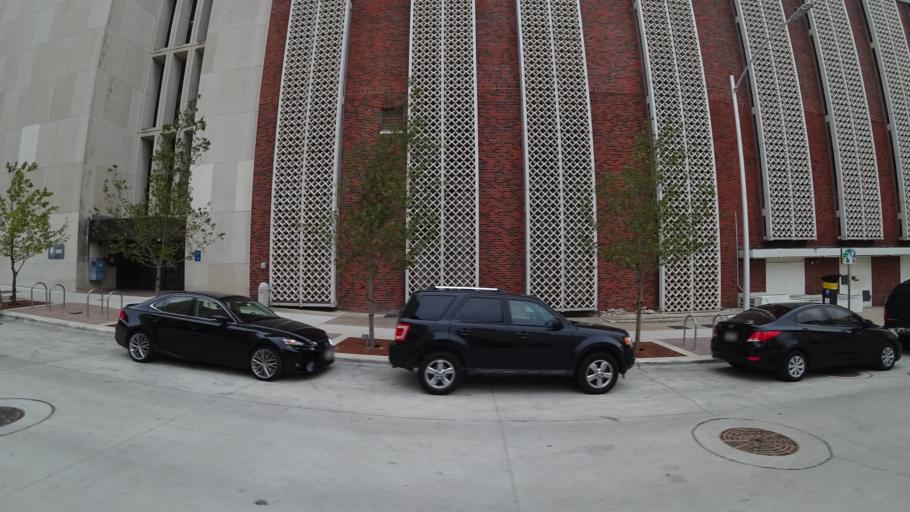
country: US
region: Texas
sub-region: Travis County
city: Austin
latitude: 30.2717
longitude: -97.7429
